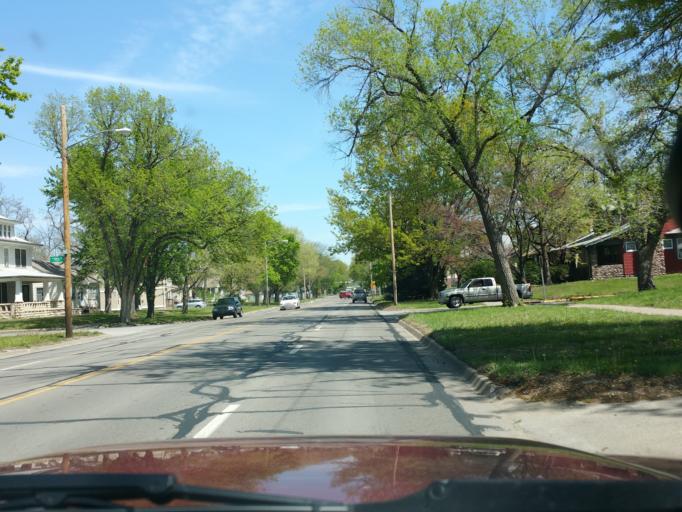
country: US
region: Kansas
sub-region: Riley County
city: Manhattan
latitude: 39.1868
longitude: -96.5706
